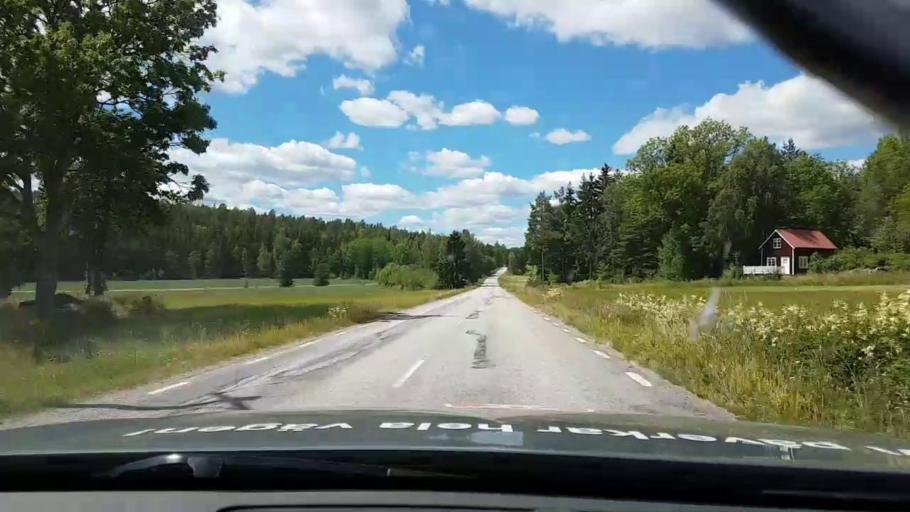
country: SE
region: Kalmar
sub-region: Vasterviks Kommun
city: Forserum
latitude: 58.0256
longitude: 16.5666
